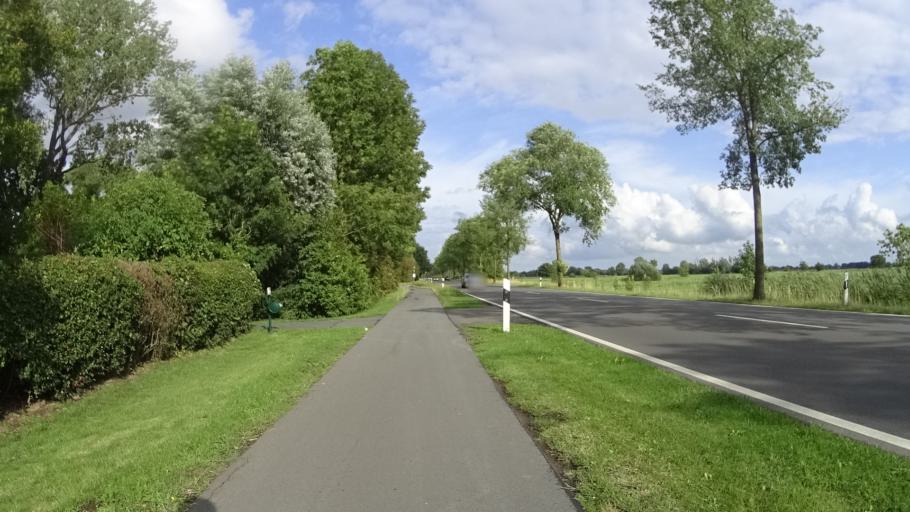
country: DE
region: Lower Saxony
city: Varel
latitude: 53.3866
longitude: 8.2156
